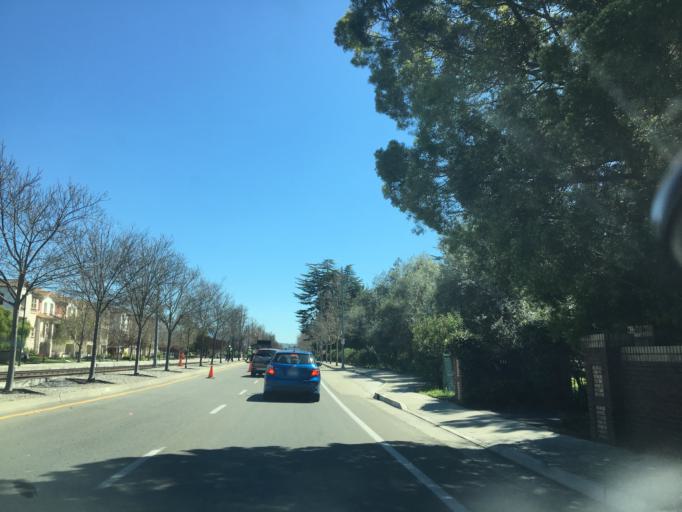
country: US
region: California
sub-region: Santa Clara County
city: Alum Rock
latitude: 37.3786
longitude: -121.8519
